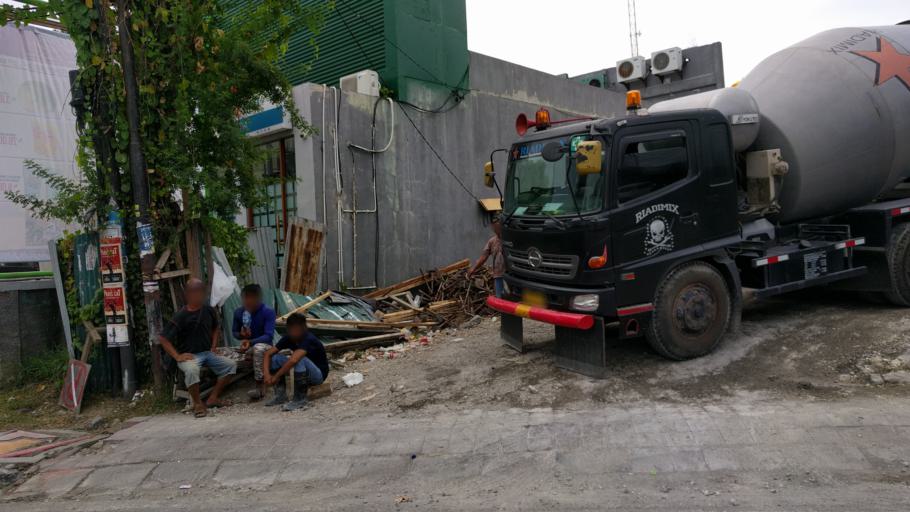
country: ID
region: Bali
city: Kuta
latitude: -8.6736
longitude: 115.1580
